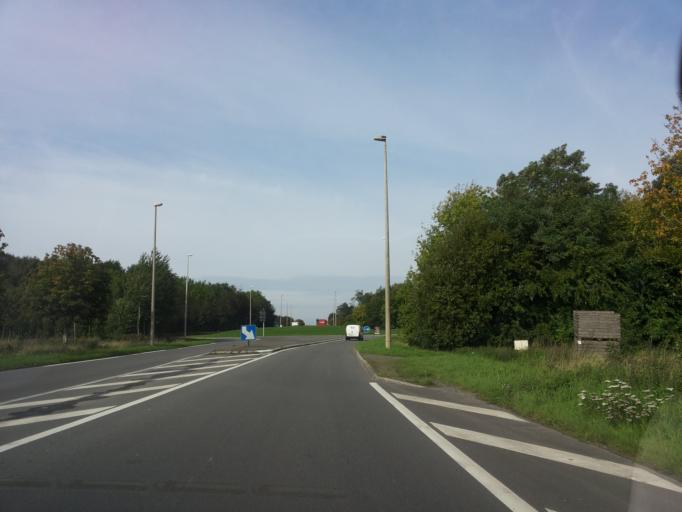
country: FR
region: Nord-Pas-de-Calais
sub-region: Departement du Pas-de-Calais
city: Tilloy-les-Mofflaines
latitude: 50.2757
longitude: 2.8317
